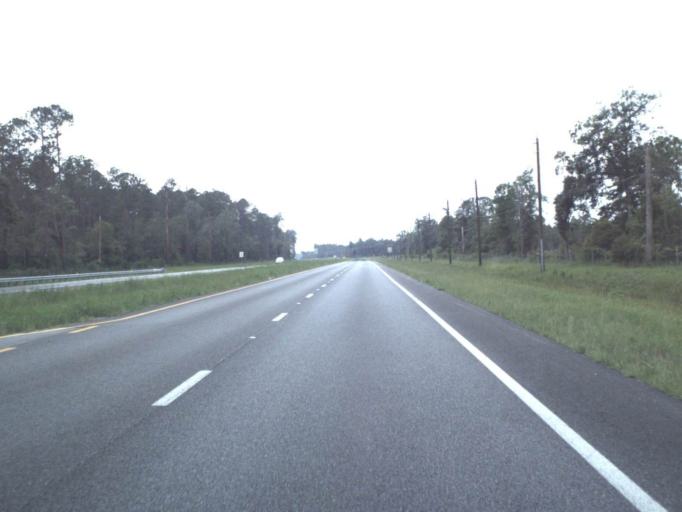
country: US
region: Florida
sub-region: Duval County
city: Baldwin
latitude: 30.4190
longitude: -81.9280
